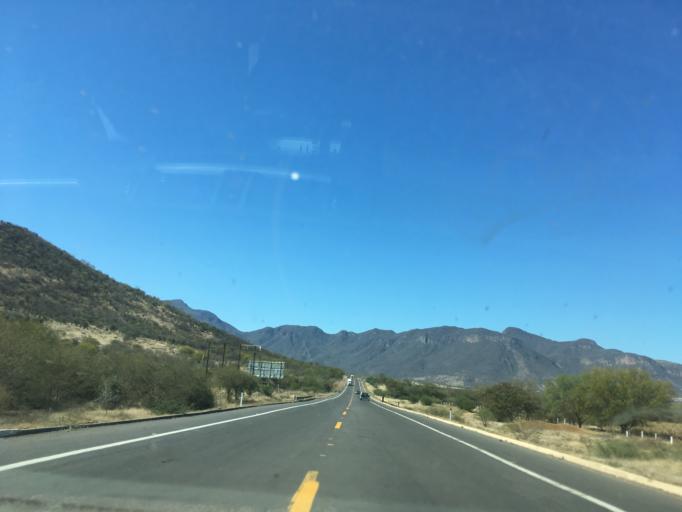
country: MX
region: Michoacan
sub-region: Arteaga
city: Las Canas
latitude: 18.6890
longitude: -102.0114
